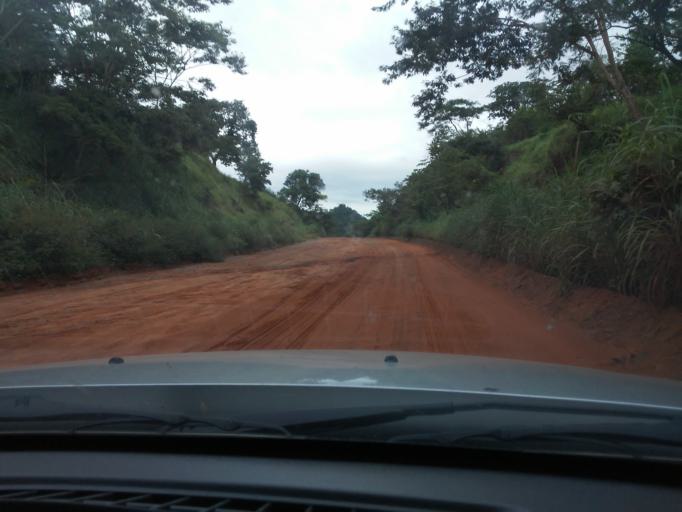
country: BR
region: Tocantins
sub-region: Taguatinga
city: Taguatinga
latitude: -12.4191
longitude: -46.4930
